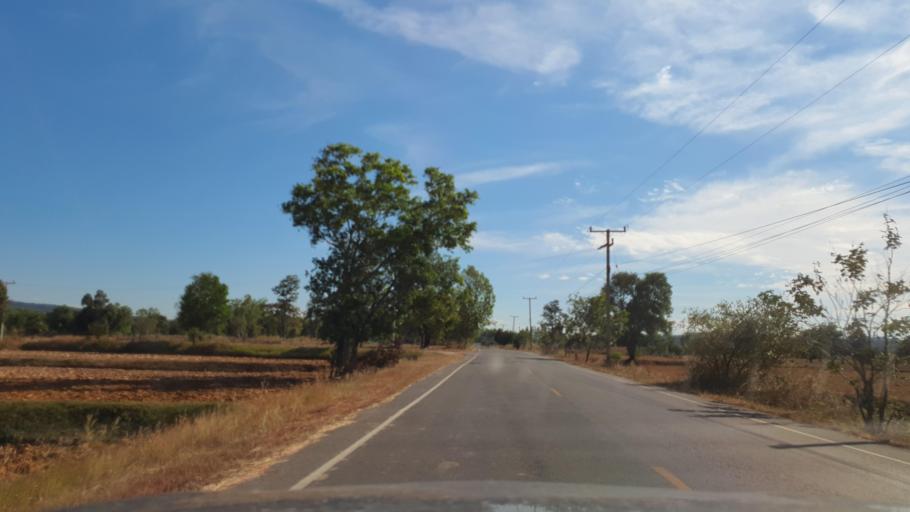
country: TH
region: Kalasin
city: Khao Wong
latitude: 16.6265
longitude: 104.1351
